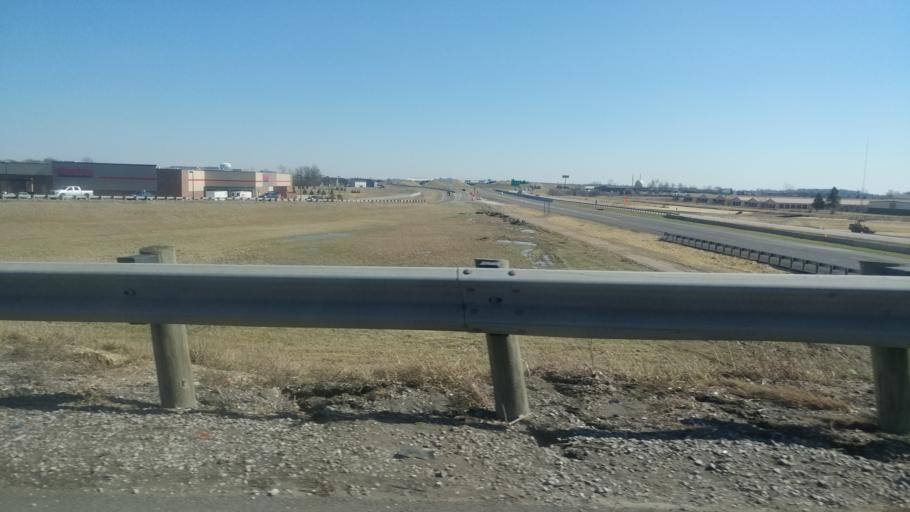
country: US
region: Ohio
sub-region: Wood County
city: Perrysburg
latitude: 41.5331
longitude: -83.6359
